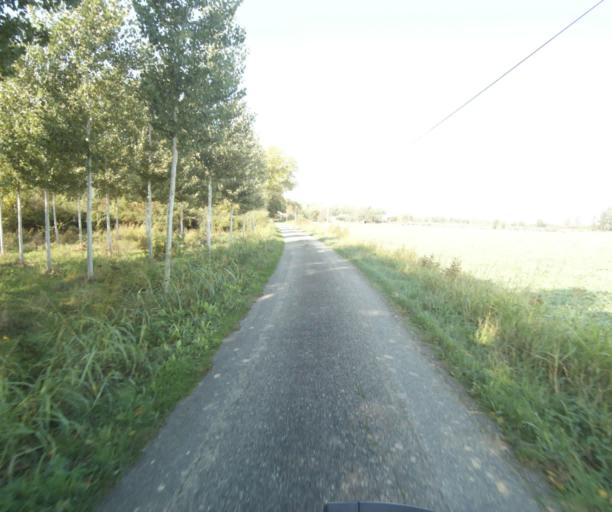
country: FR
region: Midi-Pyrenees
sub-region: Departement du Tarn-et-Garonne
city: Verdun-sur-Garonne
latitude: 43.8784
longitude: 1.2270
